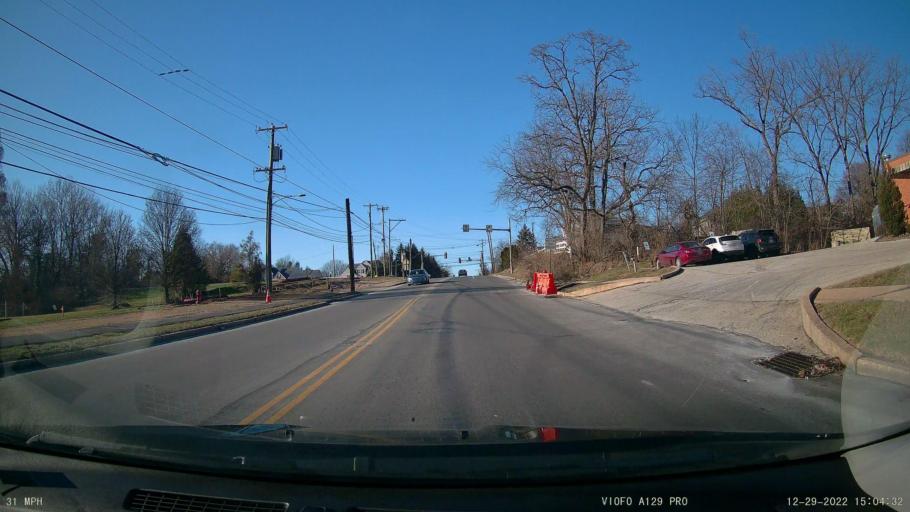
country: US
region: Pennsylvania
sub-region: Montgomery County
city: Norristown
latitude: 40.1287
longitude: -75.3229
